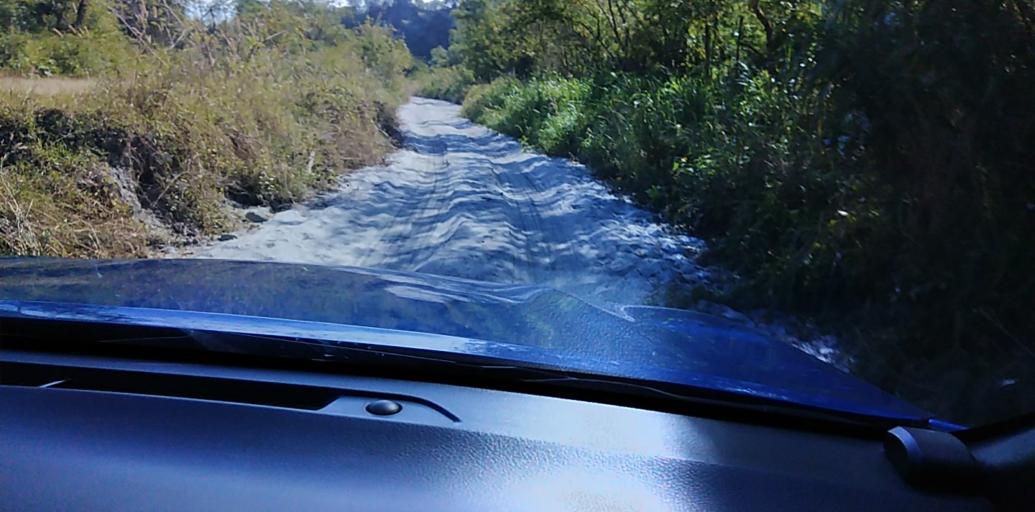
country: PH
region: Central Luzon
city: Santol
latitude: 15.1685
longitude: 120.4833
